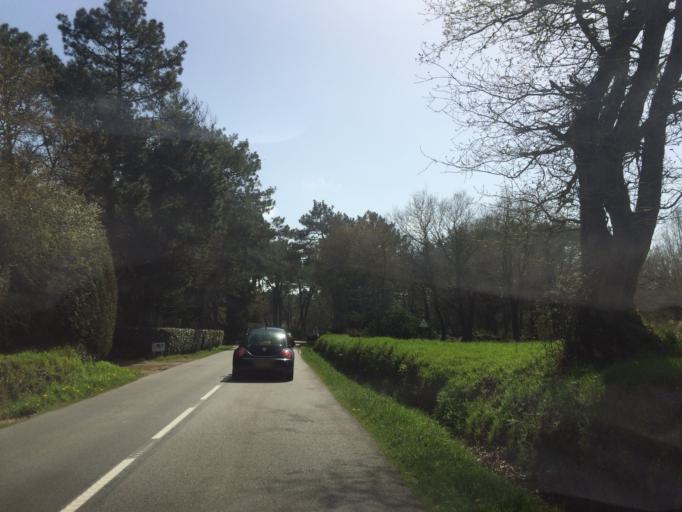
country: FR
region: Brittany
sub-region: Departement du Morbihan
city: Ploemel
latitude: 47.6290
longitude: -3.0494
